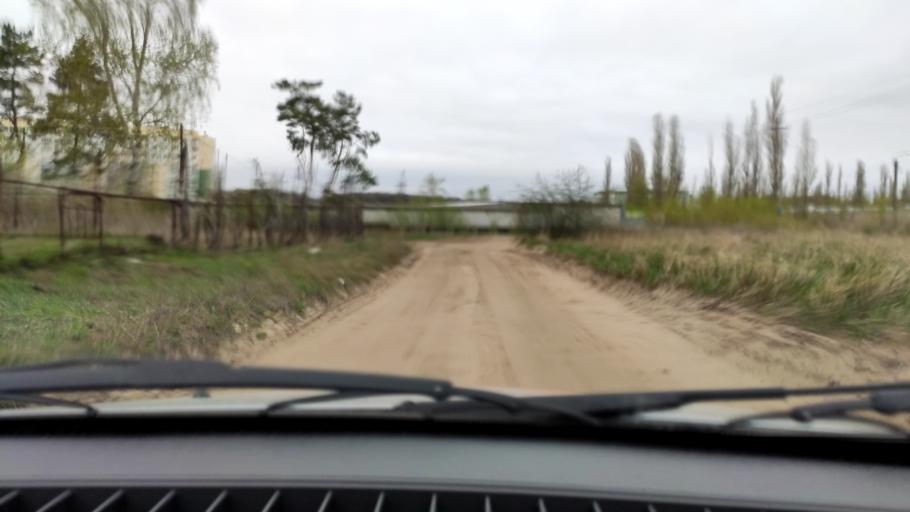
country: RU
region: Voronezj
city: Pridonskoy
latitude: 51.6196
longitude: 39.0689
